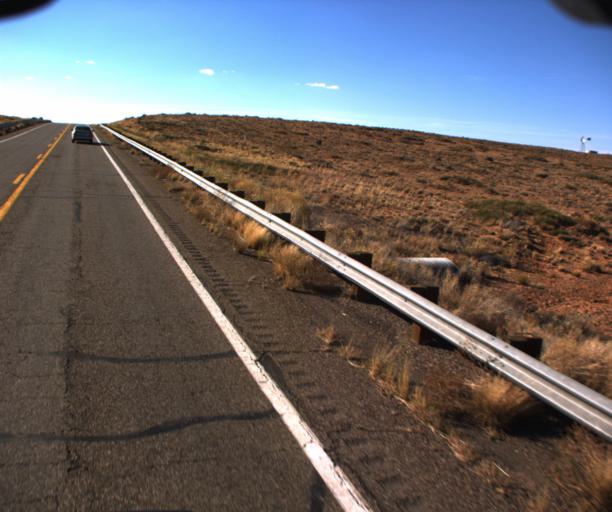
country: US
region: Arizona
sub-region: Coconino County
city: Kaibito
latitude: 36.6123
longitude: -111.0289
